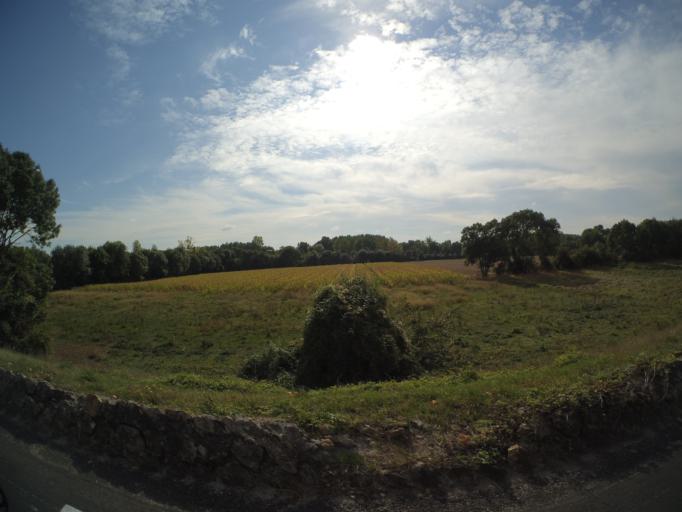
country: FR
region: Pays de la Loire
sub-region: Departement de Maine-et-Loire
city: Varennes-sur-Loire
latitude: 47.2274
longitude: 0.0797
